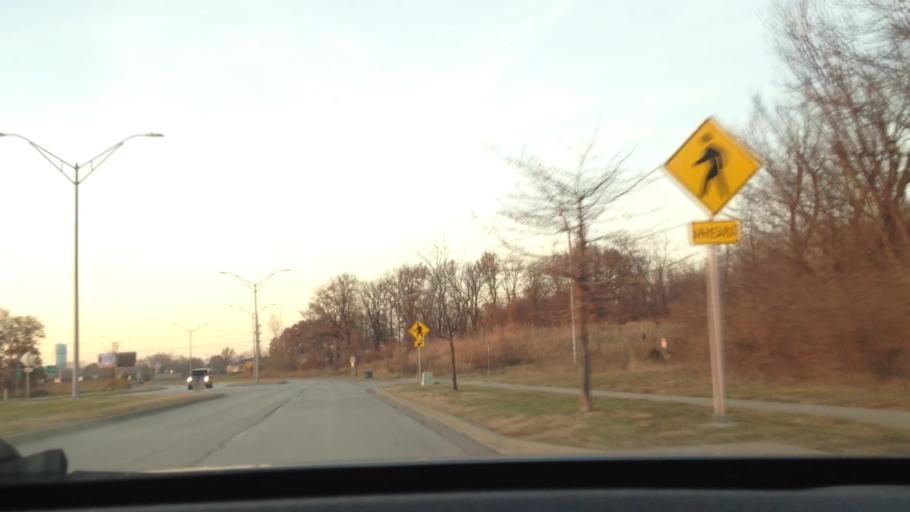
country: US
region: Missouri
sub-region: Clay County
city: Pleasant Valley
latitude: 39.2143
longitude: -94.4705
